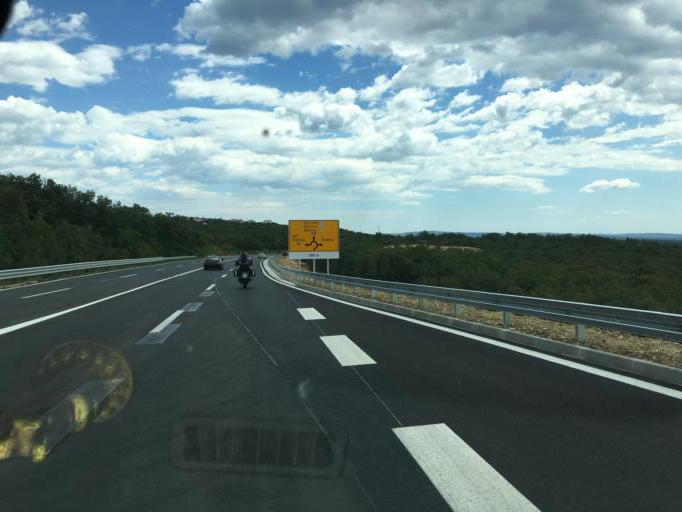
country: HR
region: Primorsko-Goranska
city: Hreljin
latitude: 45.2657
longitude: 14.5907
